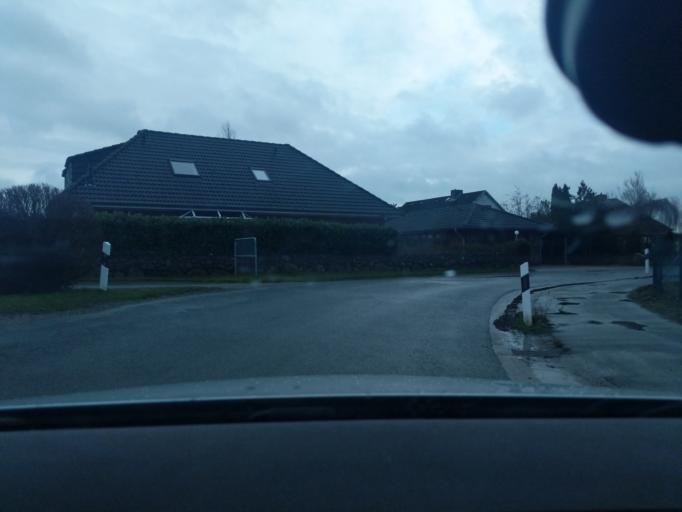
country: DE
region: Lower Saxony
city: Jork
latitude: 53.5334
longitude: 9.6526
